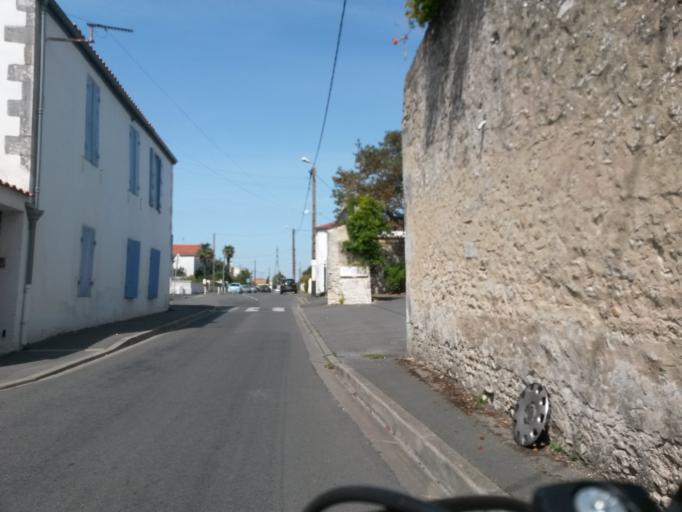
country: FR
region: Poitou-Charentes
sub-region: Departement de la Charente-Maritime
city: La Rochelle
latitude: 46.1773
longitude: -1.1409
